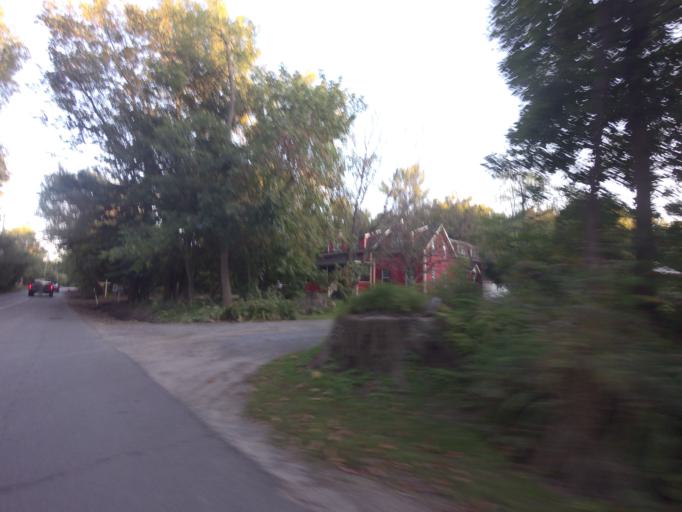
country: CA
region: Quebec
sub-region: Monteregie
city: Hudson
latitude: 45.4535
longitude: -74.1190
